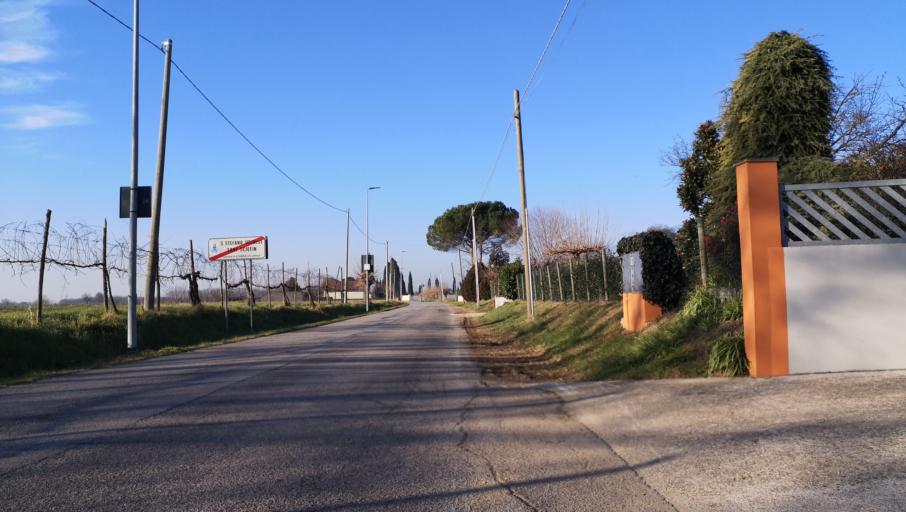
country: IT
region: Friuli Venezia Giulia
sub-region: Provincia di Udine
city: Santa Maria la Longa
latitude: 45.9547
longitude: 13.2803
